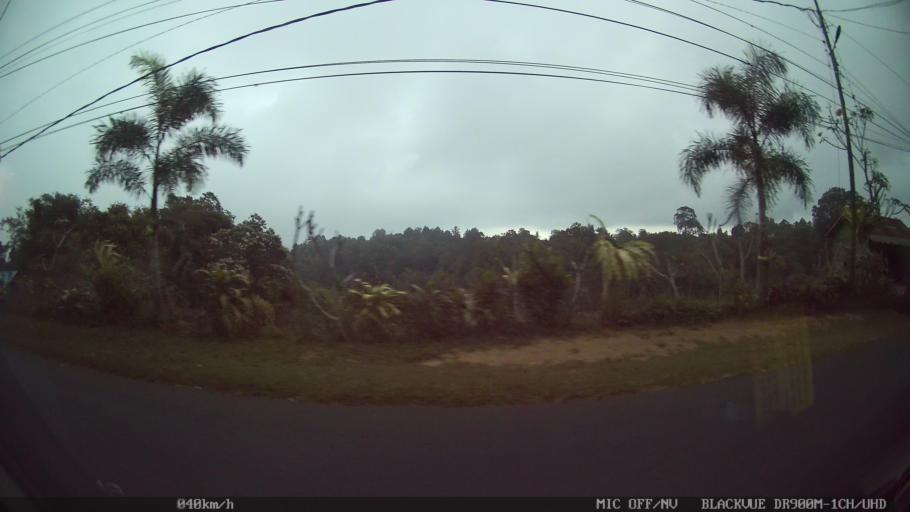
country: ID
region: Bali
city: Klau
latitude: -8.3464
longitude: 115.0295
